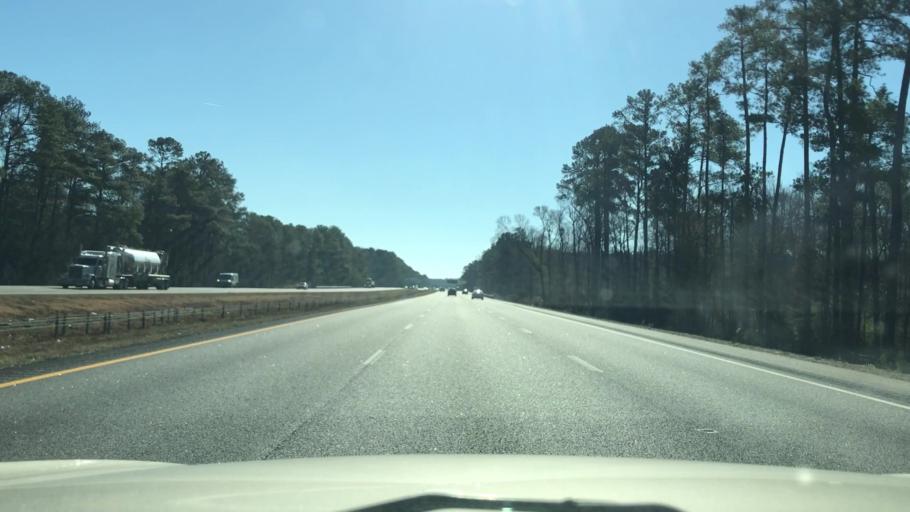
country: US
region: South Carolina
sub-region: Lexington County
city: Pineridge
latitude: 33.9040
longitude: -81.0507
